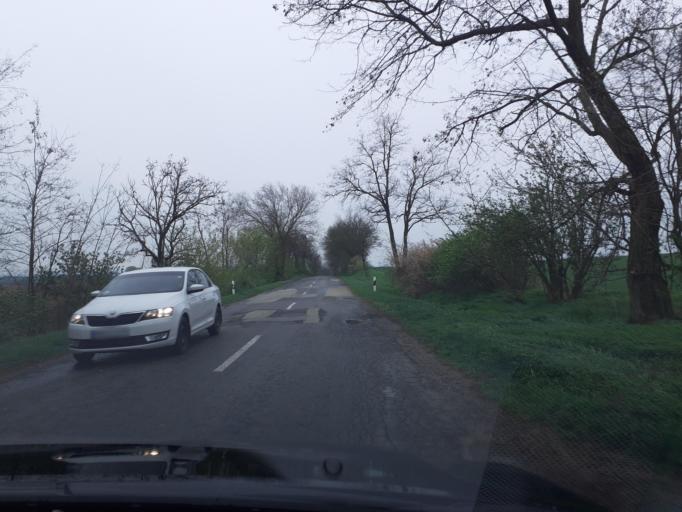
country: HU
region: Tolna
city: Hogyesz
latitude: 46.4439
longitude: 18.4601
